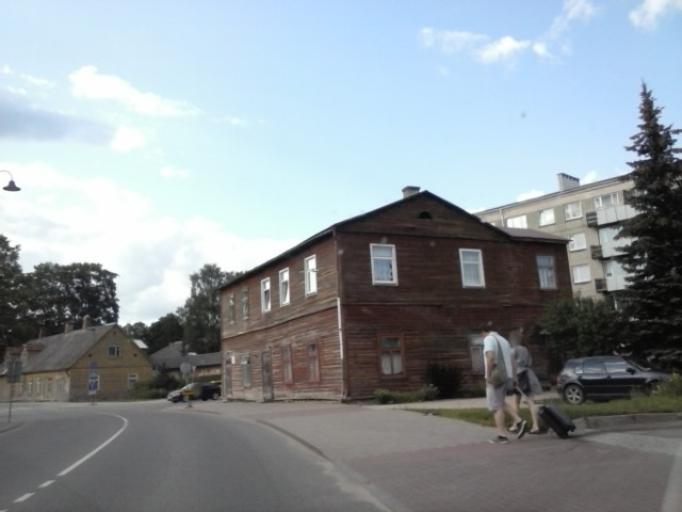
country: EE
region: Vorumaa
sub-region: Voru linn
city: Voru
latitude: 57.8411
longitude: 27.0020
